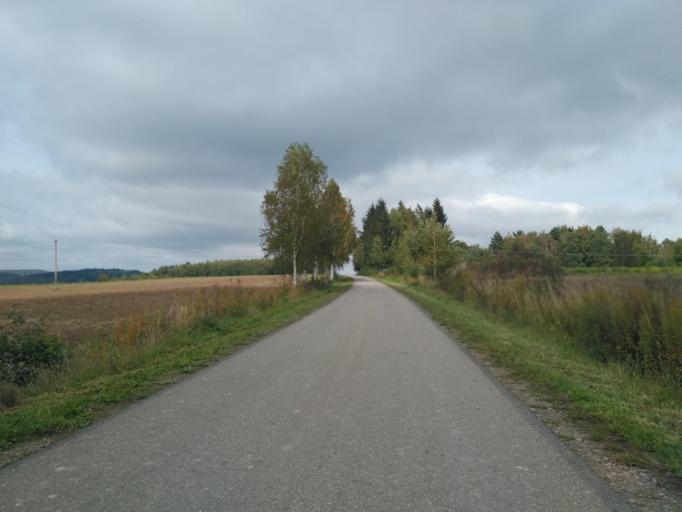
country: PL
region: Subcarpathian Voivodeship
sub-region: Powiat ropczycko-sedziszowski
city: Niedzwiada
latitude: 49.9285
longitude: 21.5039
